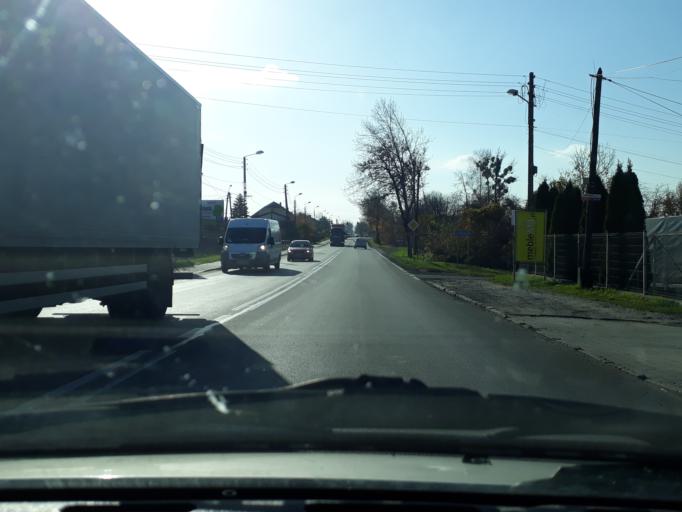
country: PL
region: Silesian Voivodeship
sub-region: Powiat tarnogorski
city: Tarnowskie Gory
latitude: 50.4348
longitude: 18.8448
